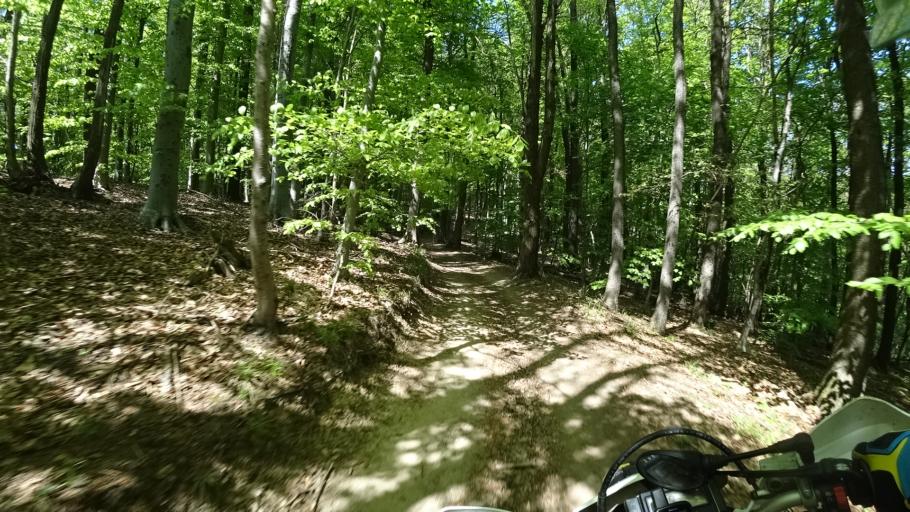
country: HR
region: Zagrebacka
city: Jablanovec
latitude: 45.8790
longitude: 15.9004
